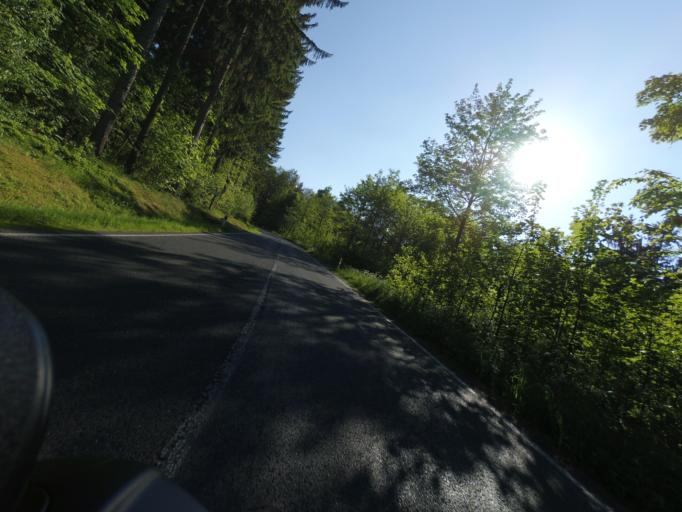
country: DE
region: Saxony
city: Bannewitz
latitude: 50.9740
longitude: 13.6870
